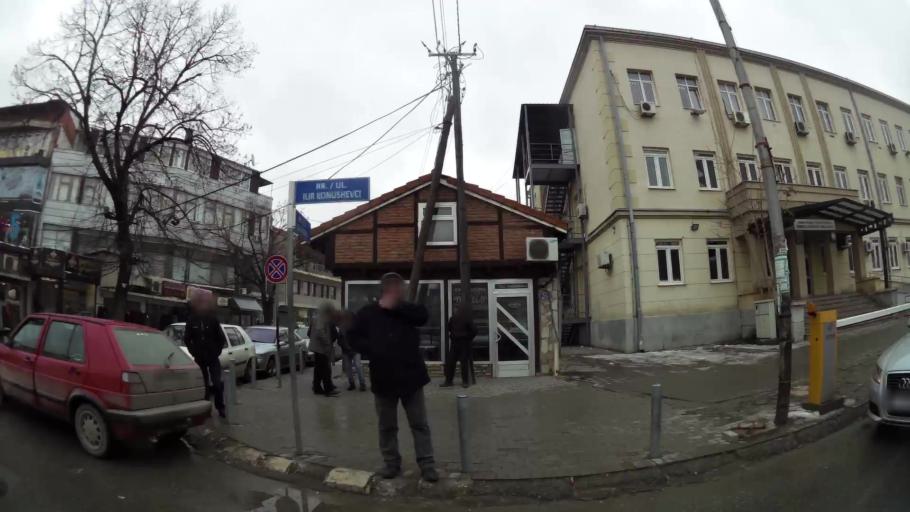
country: XK
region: Pristina
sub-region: Komuna e Prishtines
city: Pristina
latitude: 42.6682
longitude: 21.1640
